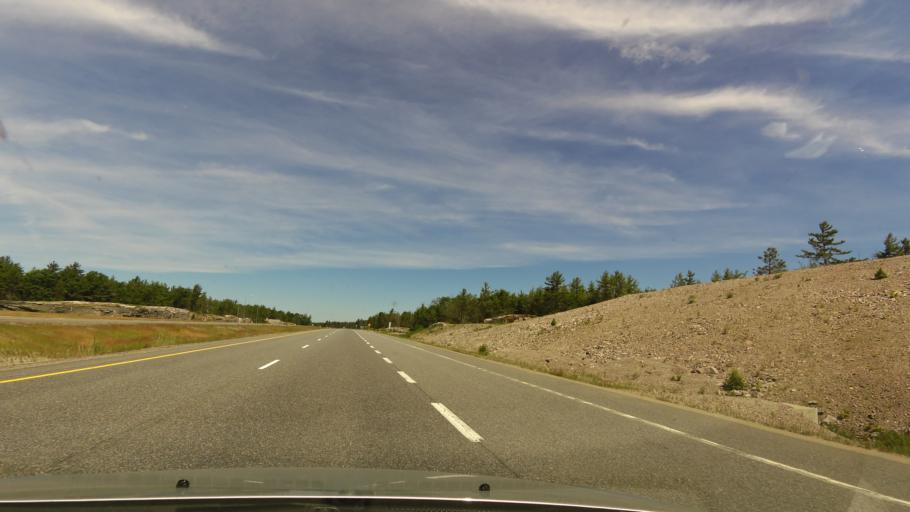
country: CA
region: Ontario
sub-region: Parry Sound District
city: Parry Sound
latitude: 45.4222
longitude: -80.0744
